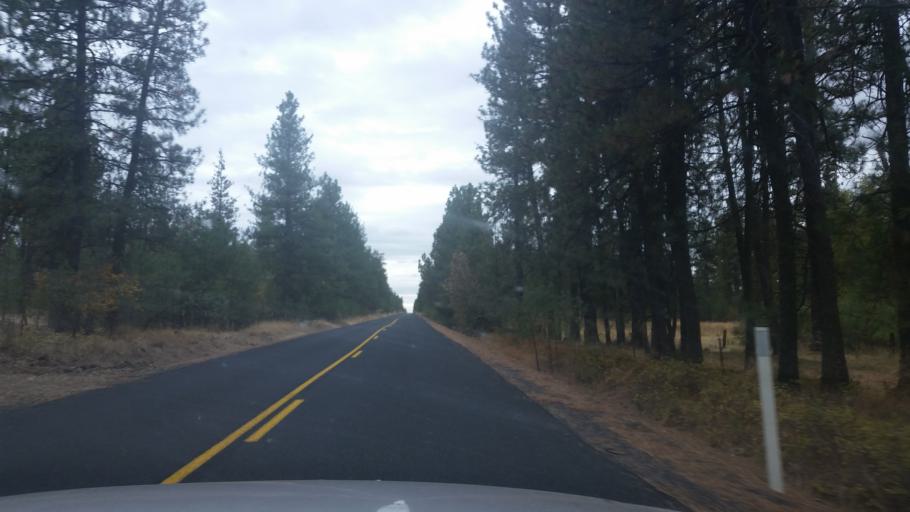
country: US
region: Washington
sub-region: Spokane County
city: Medical Lake
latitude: 47.4819
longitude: -117.7791
